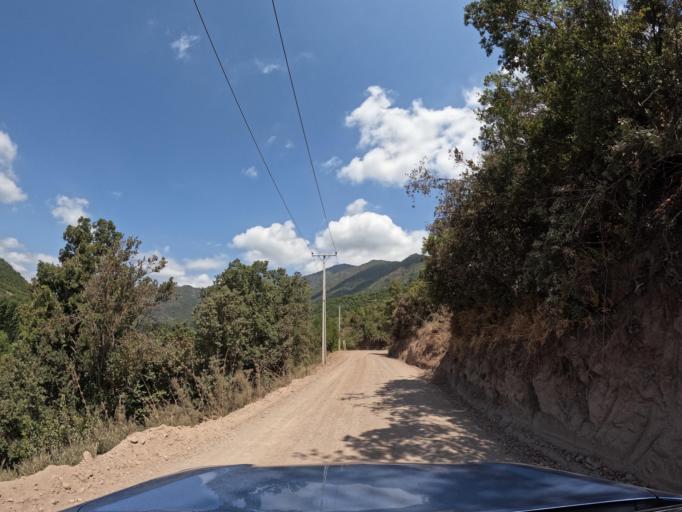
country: CL
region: Maule
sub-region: Provincia de Curico
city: Curico
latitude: -35.1188
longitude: -71.0081
